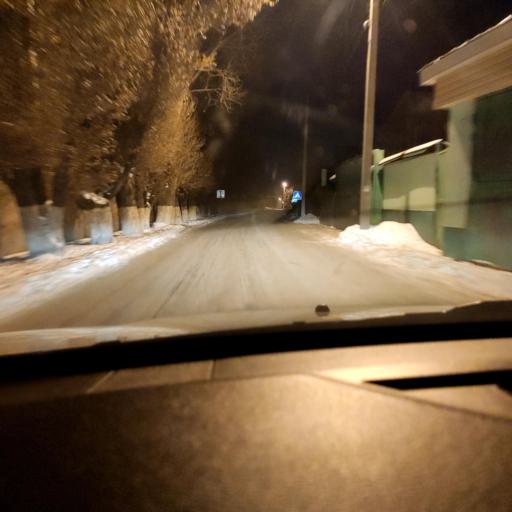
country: RU
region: Samara
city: Smyshlyayevka
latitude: 53.2503
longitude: 50.4068
